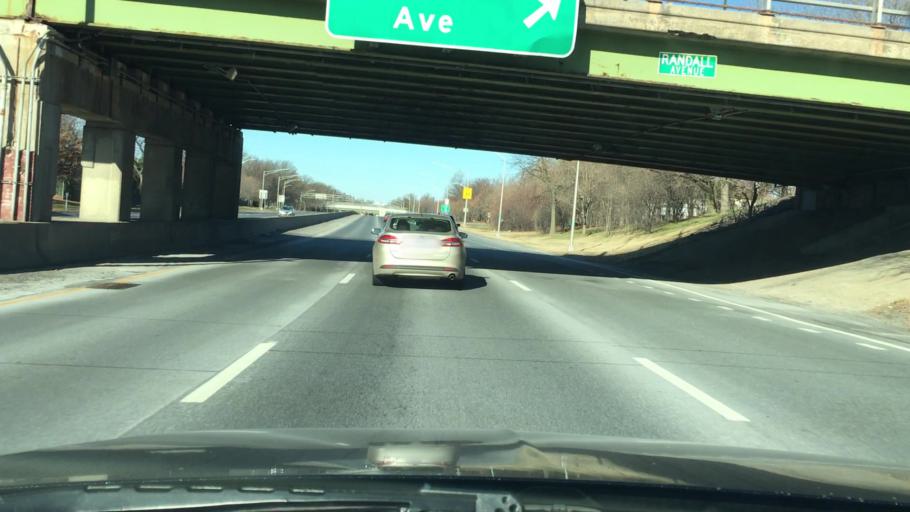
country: US
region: New York
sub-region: Bronx
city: The Bronx
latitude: 40.8280
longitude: -73.8177
